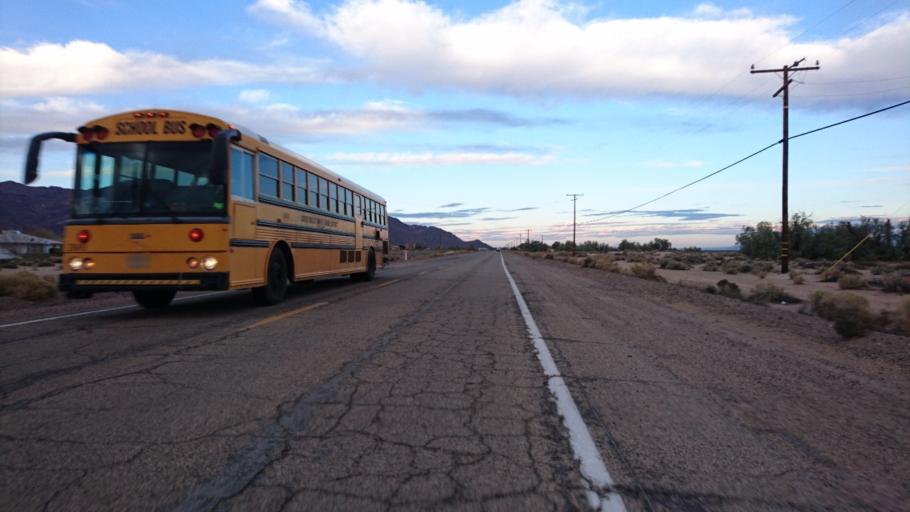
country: US
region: California
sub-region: San Bernardino County
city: Barstow
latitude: 34.8175
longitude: -116.6326
